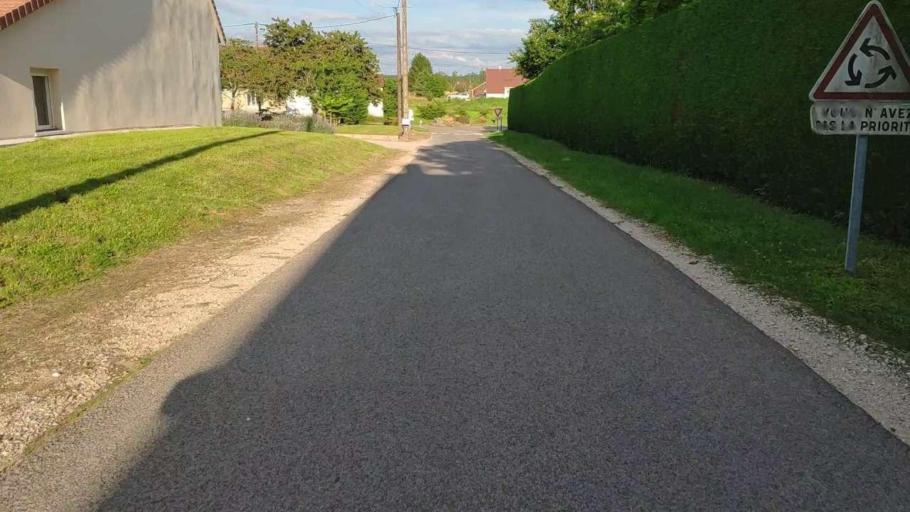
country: FR
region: Franche-Comte
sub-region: Departement du Jura
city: Bletterans
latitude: 46.7828
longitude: 5.5059
